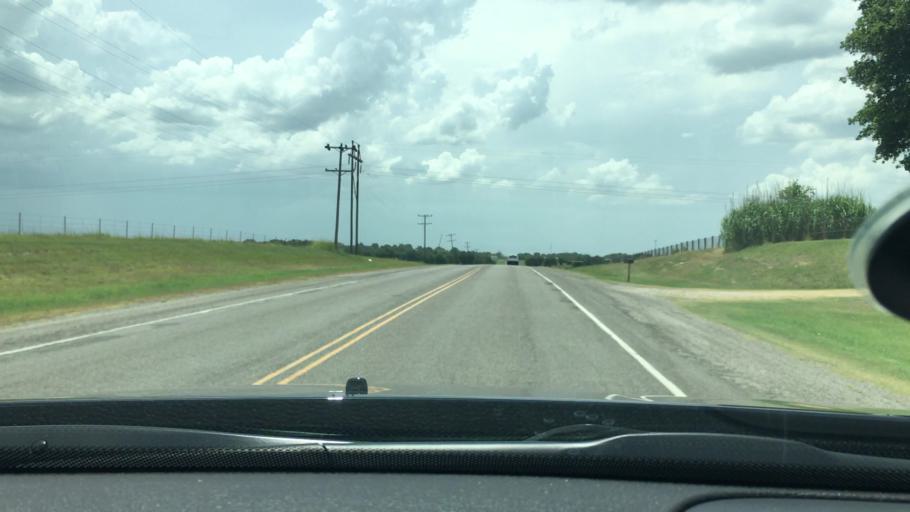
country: US
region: Oklahoma
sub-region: Love County
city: Marietta
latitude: 33.9617
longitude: -97.1263
